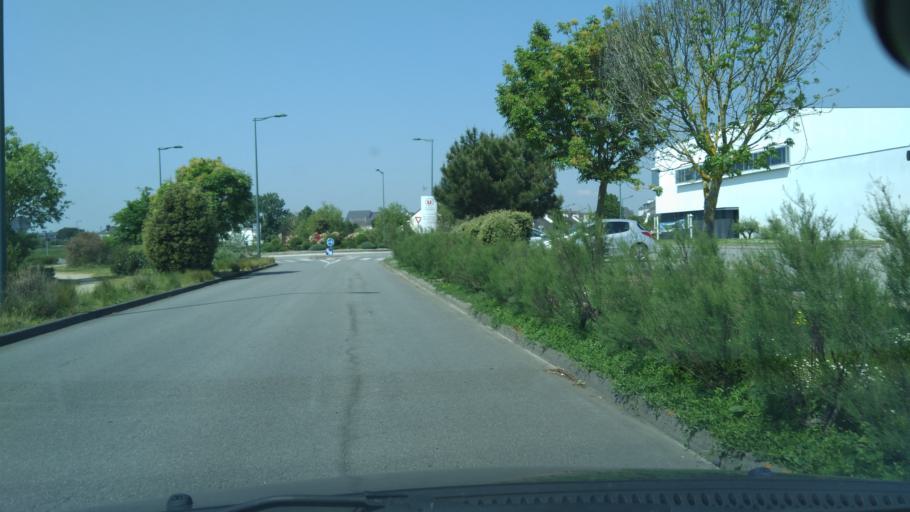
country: FR
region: Pays de la Loire
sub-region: Departement de la Loire-Atlantique
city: Montoir-de-Bretagne
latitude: 47.3255
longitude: -2.1524
